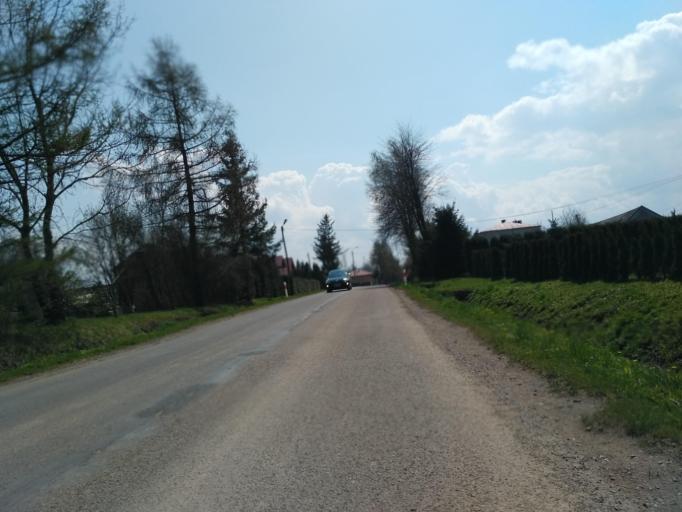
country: PL
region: Subcarpathian Voivodeship
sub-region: Powiat sanocki
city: Zarszyn
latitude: 49.5223
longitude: 21.9974
